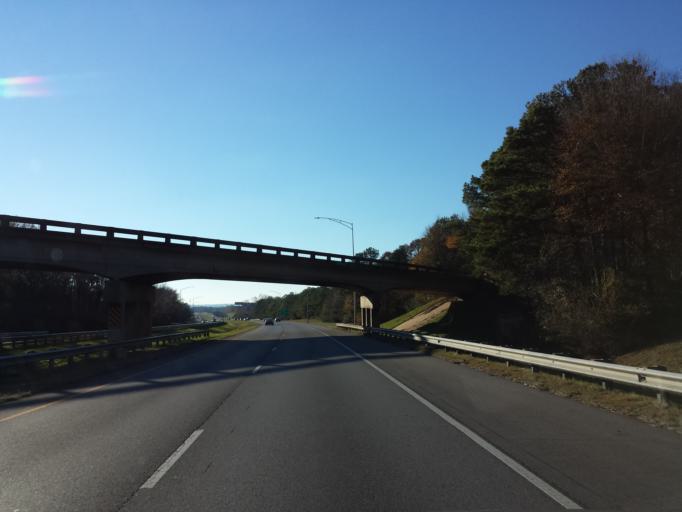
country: US
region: Alabama
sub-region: Tuscaloosa County
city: Holt
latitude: 33.1762
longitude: -87.5025
